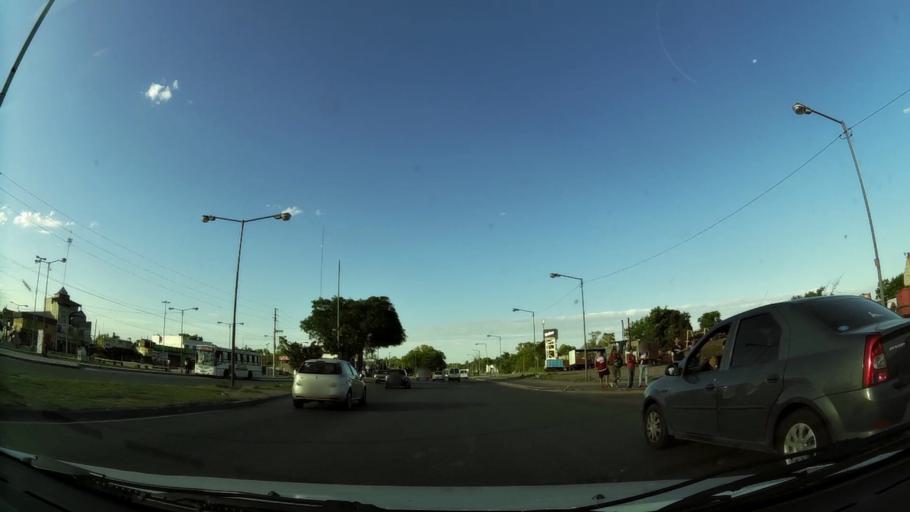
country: AR
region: Buenos Aires
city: Caseros
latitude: -34.5540
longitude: -58.5850
